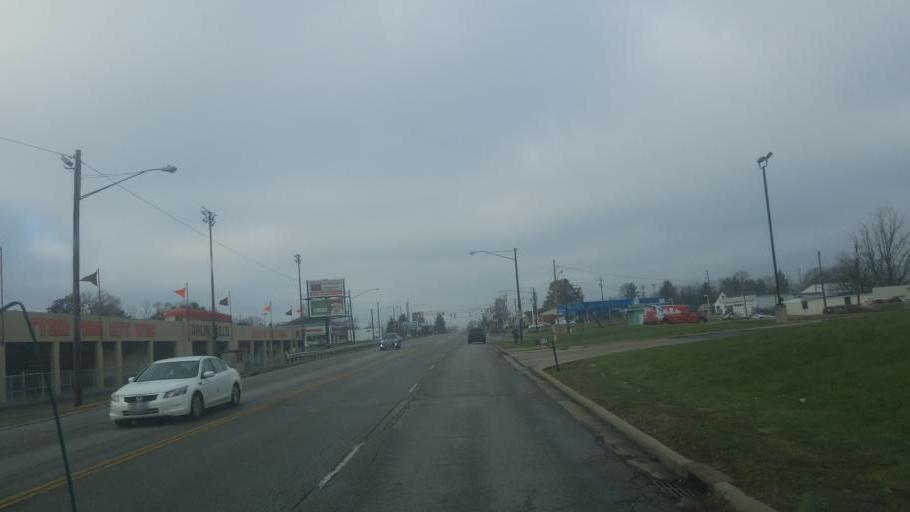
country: US
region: Ohio
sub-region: Richland County
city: Mansfield
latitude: 40.7655
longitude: -82.5495
